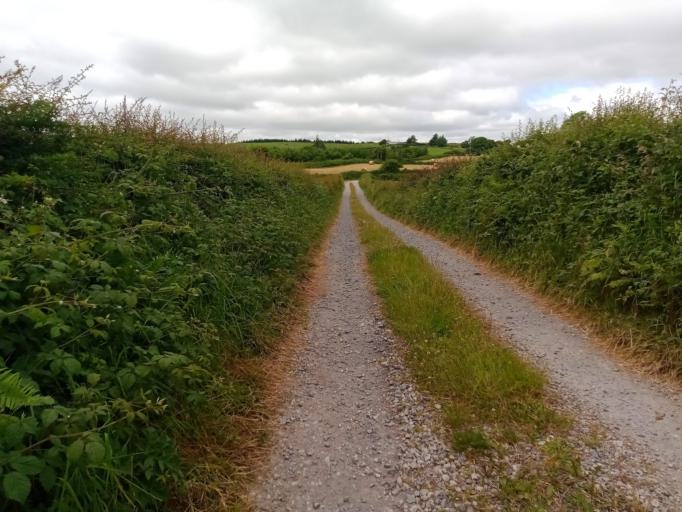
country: IE
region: Leinster
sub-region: Kilkenny
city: Ballyragget
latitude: 52.7940
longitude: -7.4622
